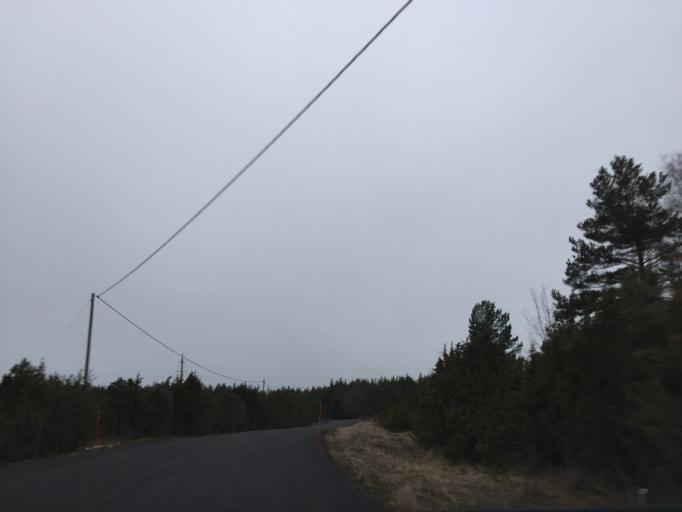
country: EE
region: Laeaene
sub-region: Lihula vald
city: Lihula
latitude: 58.6576
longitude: 23.5890
